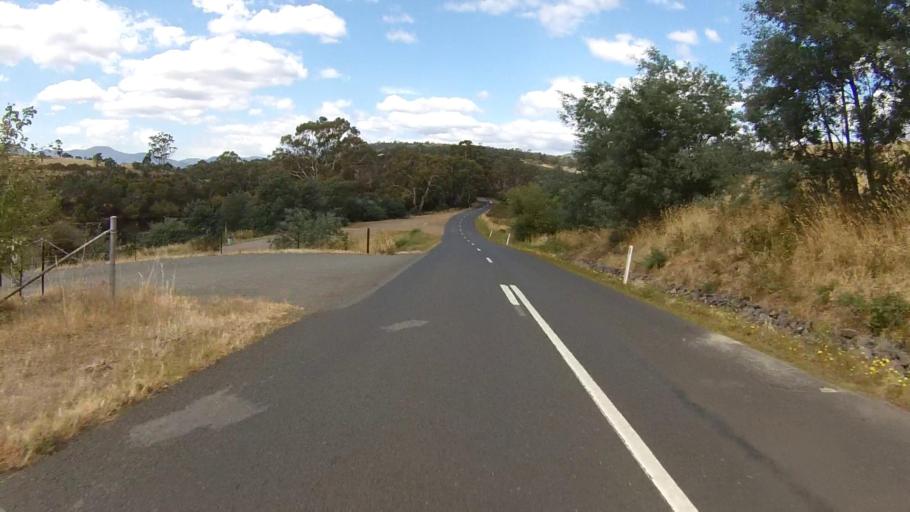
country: AU
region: Tasmania
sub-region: Derwent Valley
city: New Norfolk
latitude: -42.7549
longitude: 146.9844
